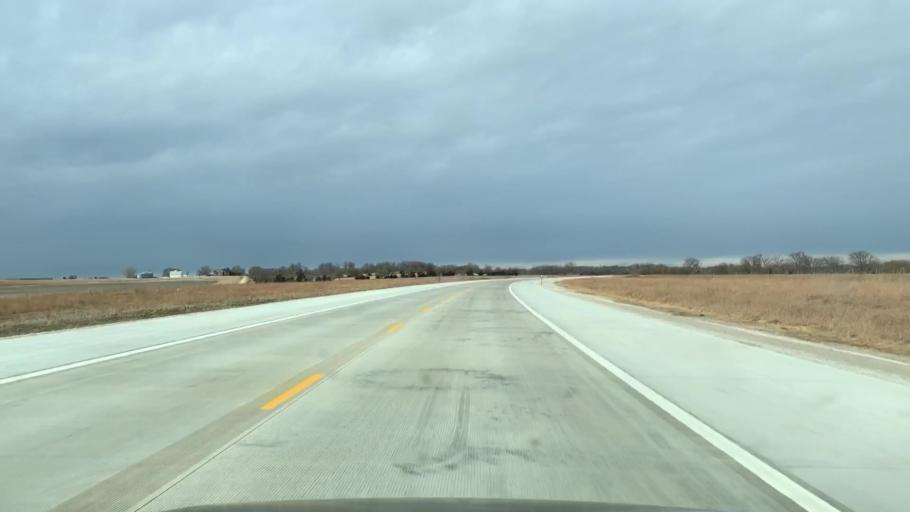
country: US
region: Kansas
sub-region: Allen County
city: Humboldt
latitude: 37.8539
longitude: -95.4091
